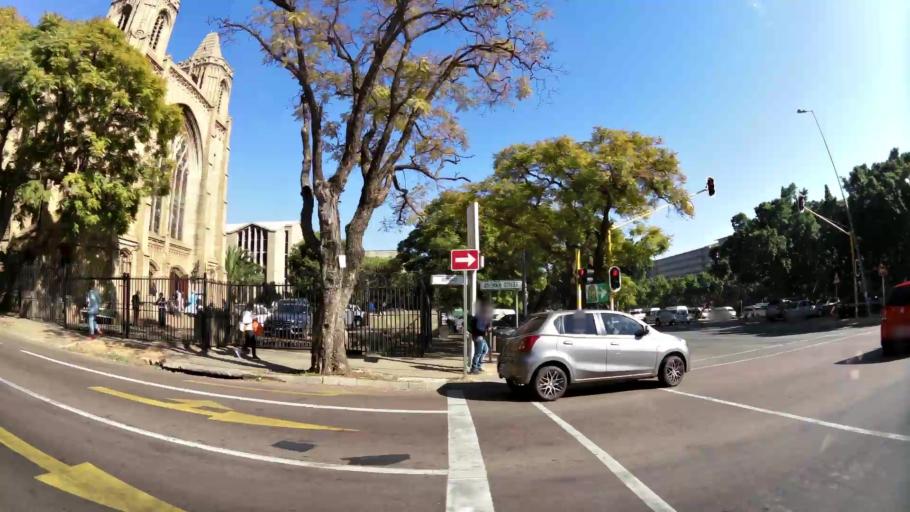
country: ZA
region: Gauteng
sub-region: City of Tshwane Metropolitan Municipality
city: Pretoria
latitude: -25.7511
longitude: 28.1859
